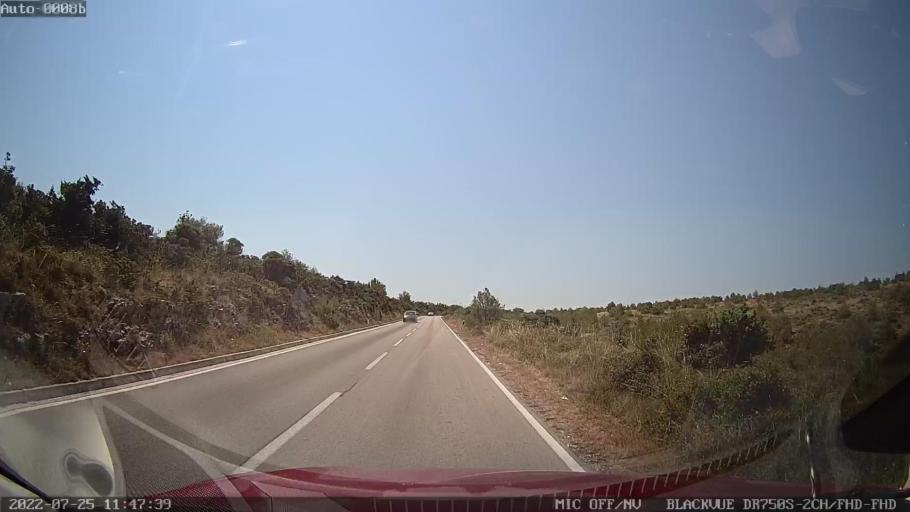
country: HR
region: Zadarska
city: Razanac
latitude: 44.2366
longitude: 15.3023
